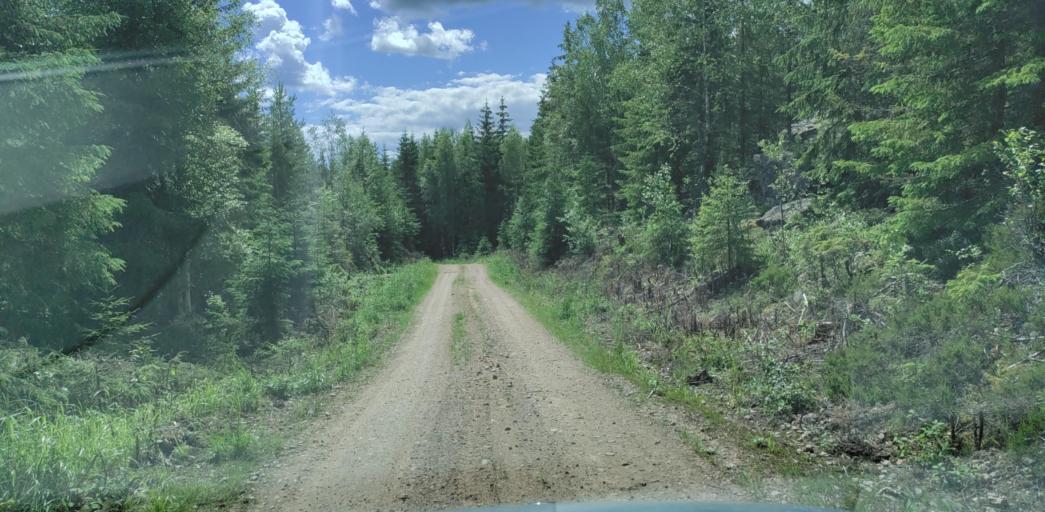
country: SE
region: Vaermland
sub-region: Hagfors Kommun
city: Ekshaerad
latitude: 60.1112
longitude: 13.3251
